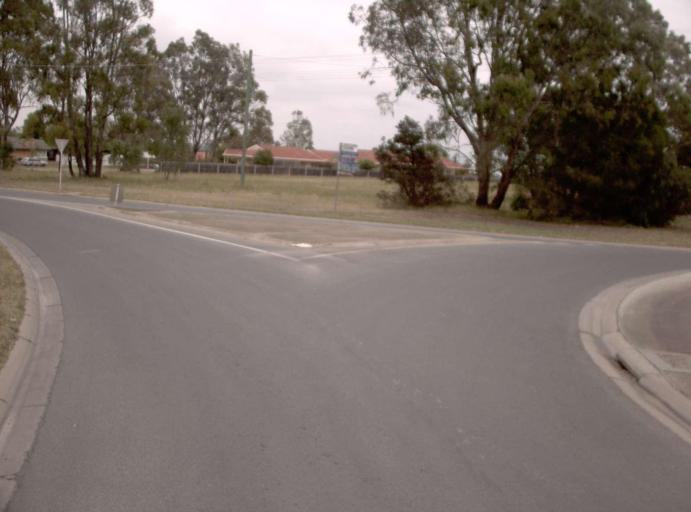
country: AU
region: Victoria
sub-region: Wellington
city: Heyfield
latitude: -37.9786
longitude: 146.7845
